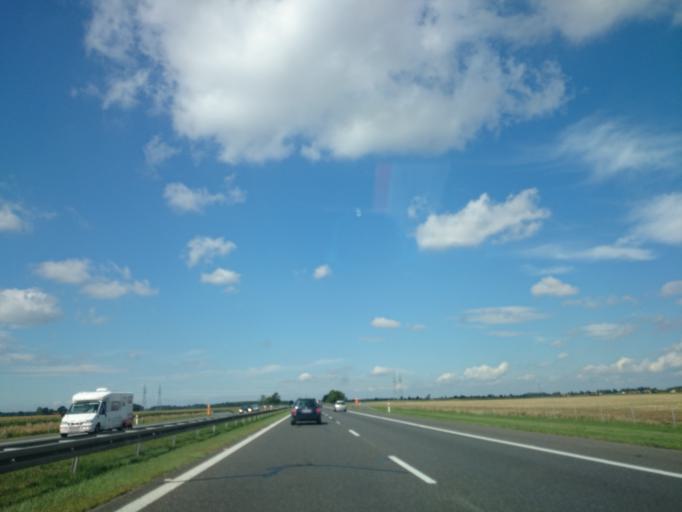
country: PL
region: Opole Voivodeship
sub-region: Powiat brzeski
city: Lewin Brzeski
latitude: 50.7134
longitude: 17.5788
